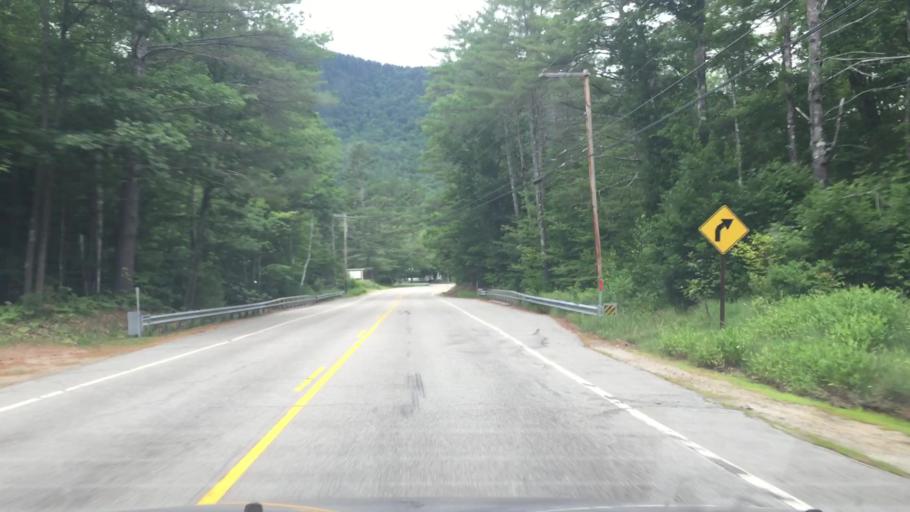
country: US
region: New Hampshire
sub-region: Carroll County
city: North Conway
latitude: 44.0741
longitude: -71.2999
